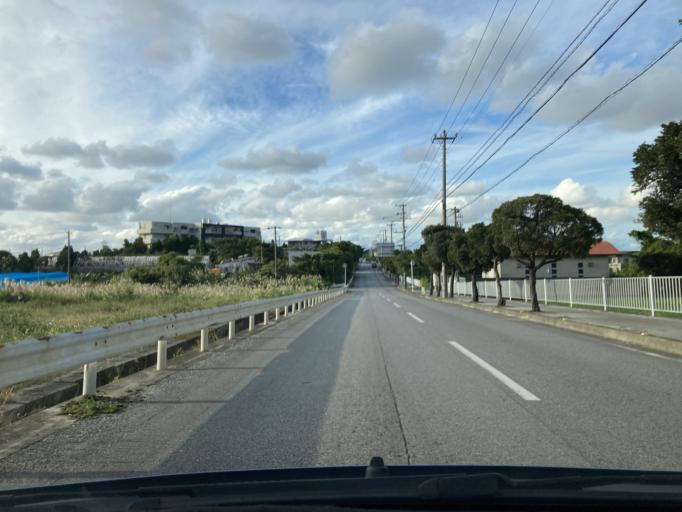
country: JP
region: Okinawa
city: Itoman
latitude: 26.1399
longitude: 127.7363
